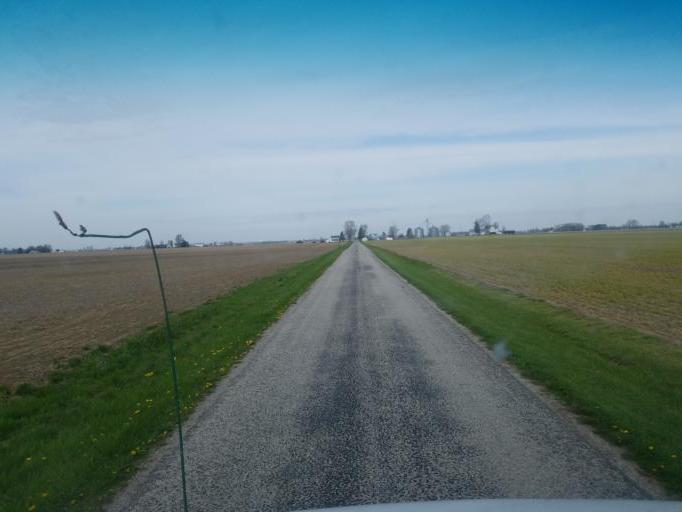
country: US
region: Ohio
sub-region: Marion County
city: Prospect
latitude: 40.4333
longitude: -83.2290
